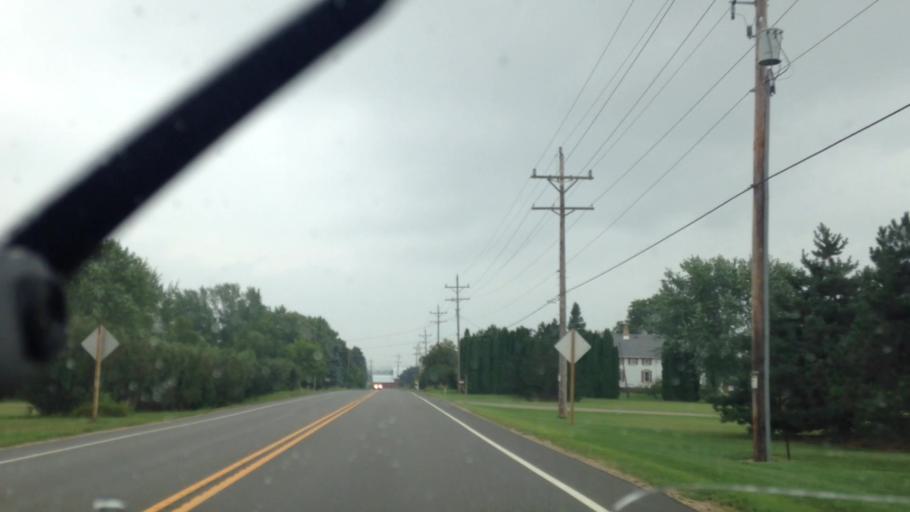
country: US
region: Wisconsin
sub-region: Washington County
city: Richfield
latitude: 43.2790
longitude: -88.2106
